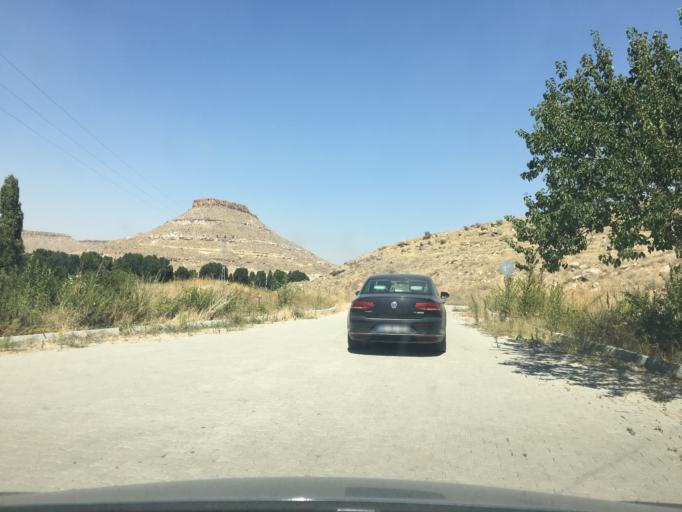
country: TR
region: Kayseri
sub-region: Yesilhisar
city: Yesilhisar
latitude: 38.4645
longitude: 34.9656
